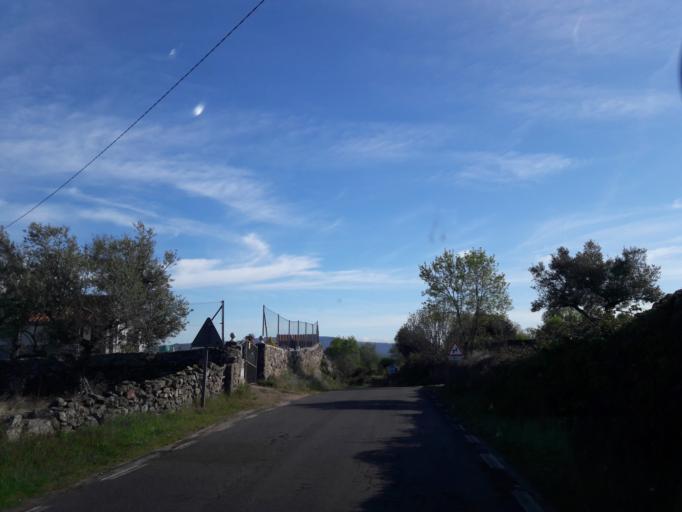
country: ES
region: Castille and Leon
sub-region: Provincia de Salamanca
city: Navalmoral de Bejar
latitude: 40.4270
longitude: -5.7833
